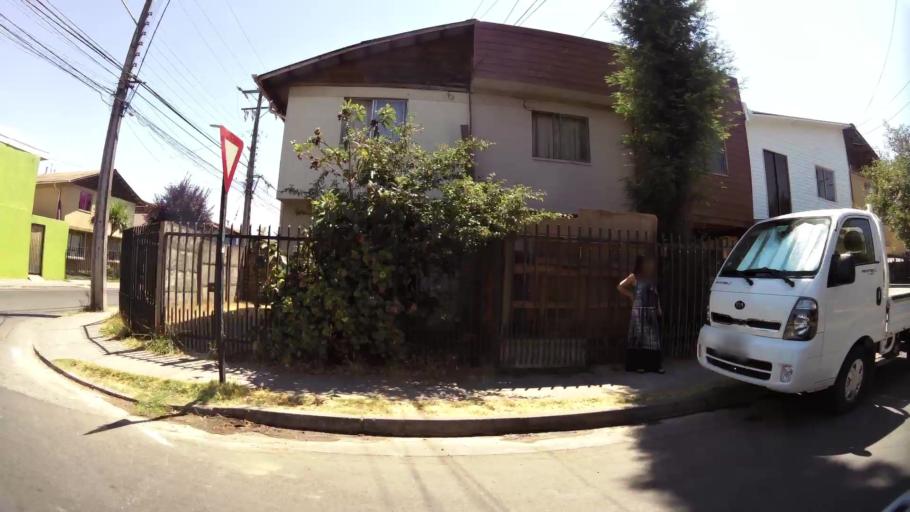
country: CL
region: Maule
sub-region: Provincia de Curico
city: Curico
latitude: -34.9683
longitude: -71.2212
